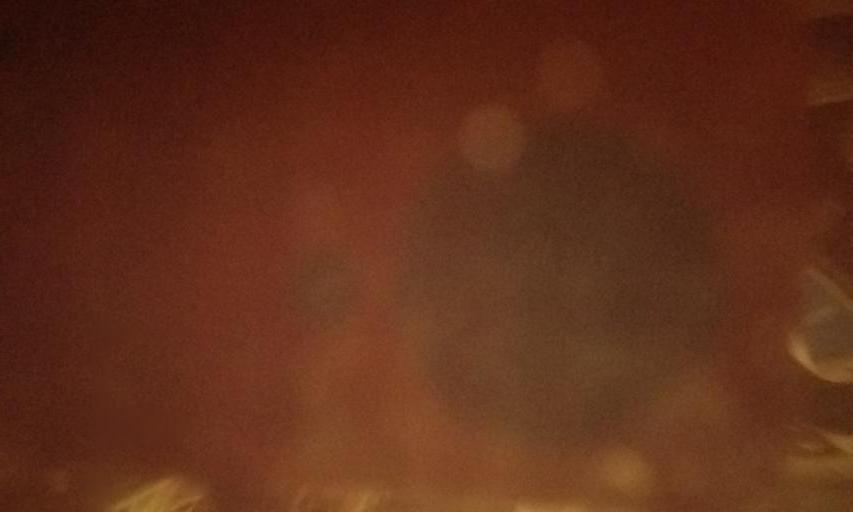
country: JP
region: Hyogo
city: Ashiya
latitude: 34.7341
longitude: 135.2705
